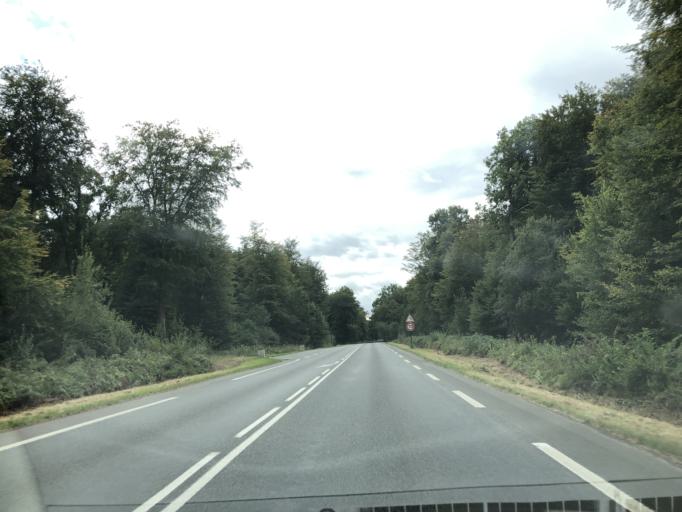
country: FR
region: Nord-Pas-de-Calais
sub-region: Departement du Pas-de-Calais
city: Hesdin
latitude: 50.3952
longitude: 2.0421
